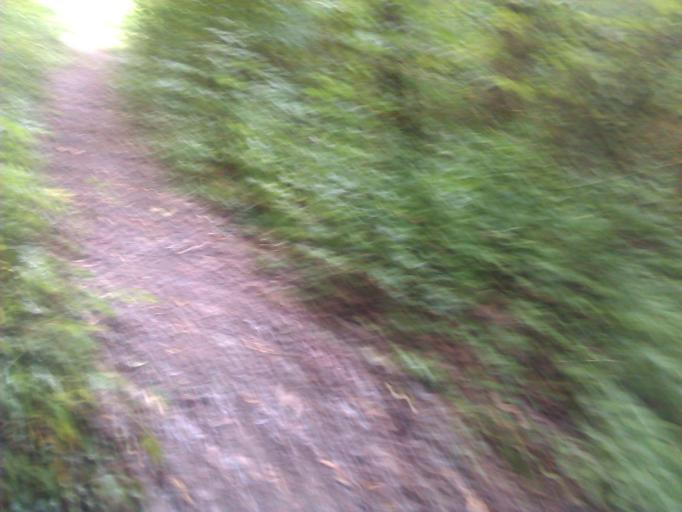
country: DE
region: Baden-Wuerttemberg
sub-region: Tuebingen Region
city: Kirchentellinsfurt
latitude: 48.5411
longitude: 9.1470
